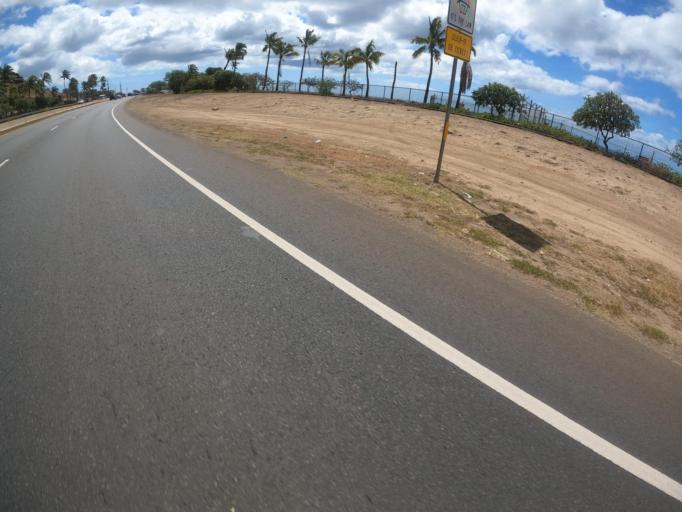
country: US
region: Hawaii
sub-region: Honolulu County
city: Makakilo
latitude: 21.3556
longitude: -158.1293
